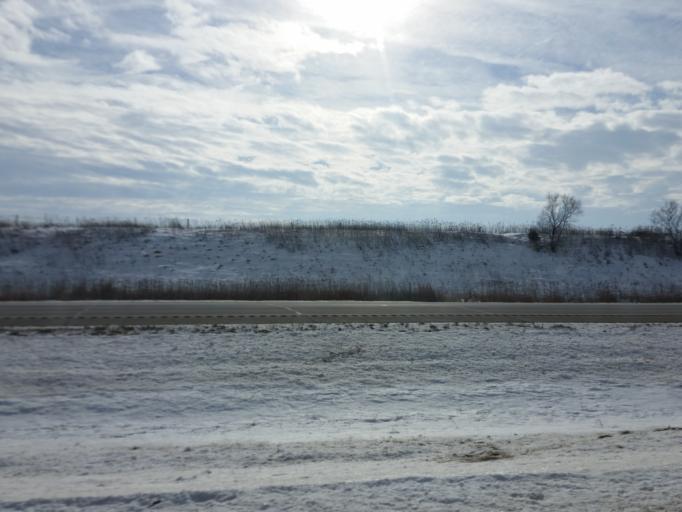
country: US
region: Iowa
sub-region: Buchanan County
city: Independence
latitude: 42.4618
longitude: -91.7592
